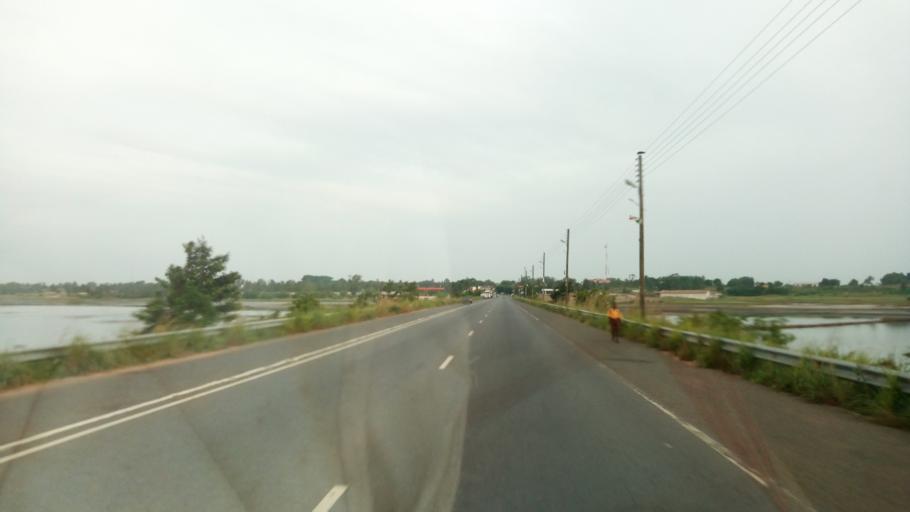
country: TG
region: Maritime
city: Lome
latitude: 6.1119
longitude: 1.1381
